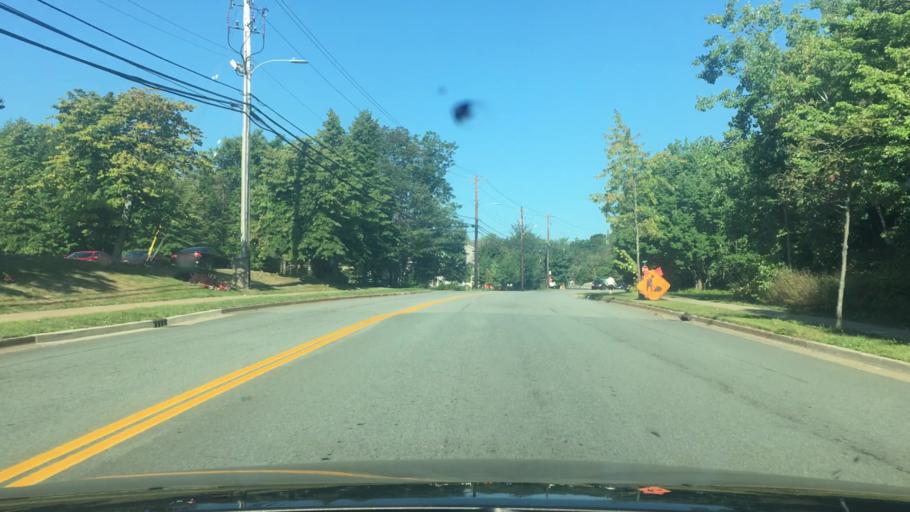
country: CA
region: Nova Scotia
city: Dartmouth
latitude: 44.7157
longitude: -63.6803
